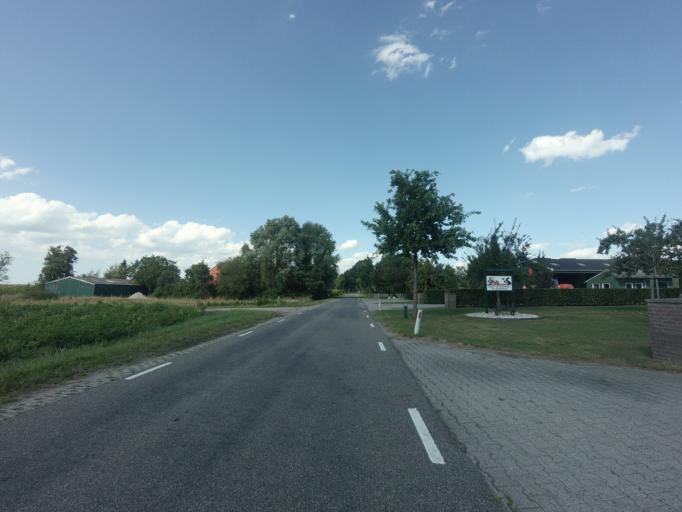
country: NL
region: Drenthe
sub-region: Gemeente Hoogeveen
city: Hoogeveen
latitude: 52.6393
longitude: 6.4927
